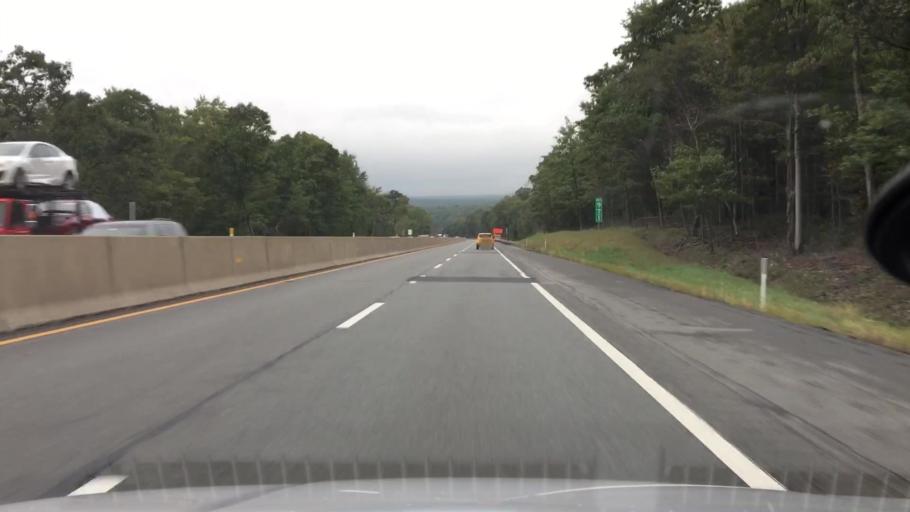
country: US
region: Pennsylvania
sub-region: Luzerne County
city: White Haven
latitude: 41.0919
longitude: -75.7406
